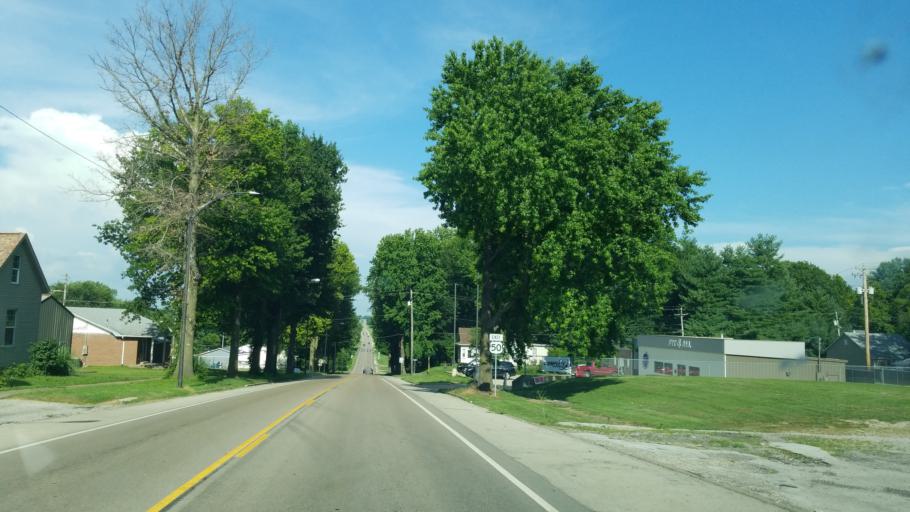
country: US
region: Illinois
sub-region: Saint Clair County
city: Lebanon
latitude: 38.6039
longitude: -89.8061
